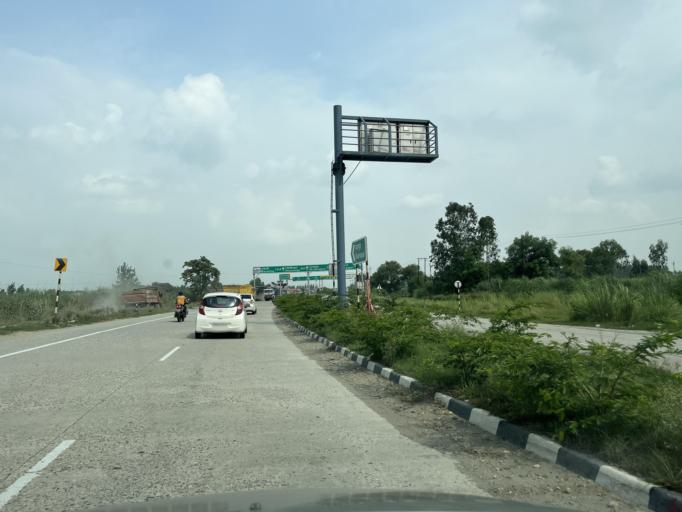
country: IN
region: Uttarakhand
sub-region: Udham Singh Nagar
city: Bazpur
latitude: 29.1498
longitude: 79.0845
